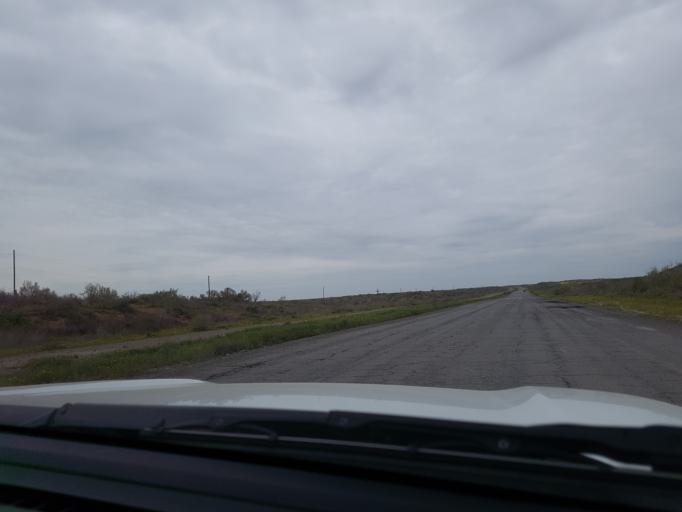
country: TM
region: Mary
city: Bayramaly
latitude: 37.9053
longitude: 62.6191
